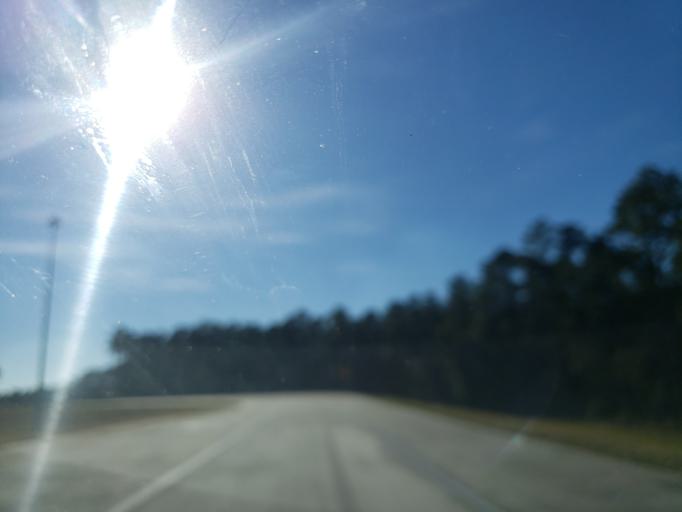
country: US
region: Georgia
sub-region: McIntosh County
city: Darien
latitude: 31.3067
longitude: -81.4814
